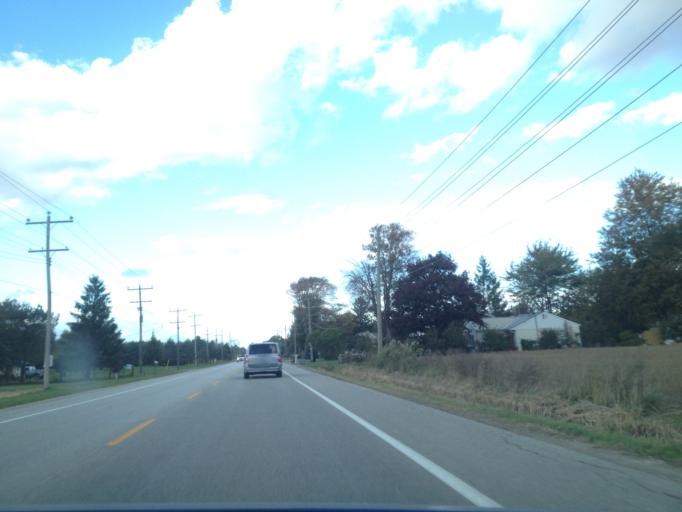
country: CA
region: Ontario
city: Amherstburg
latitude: 42.0737
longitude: -82.7369
